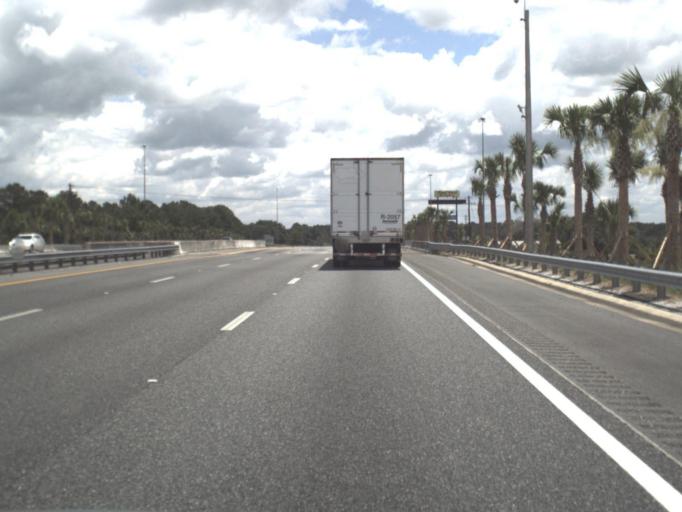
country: US
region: Florida
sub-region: Alachua County
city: High Springs
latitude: 30.0001
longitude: -82.5983
